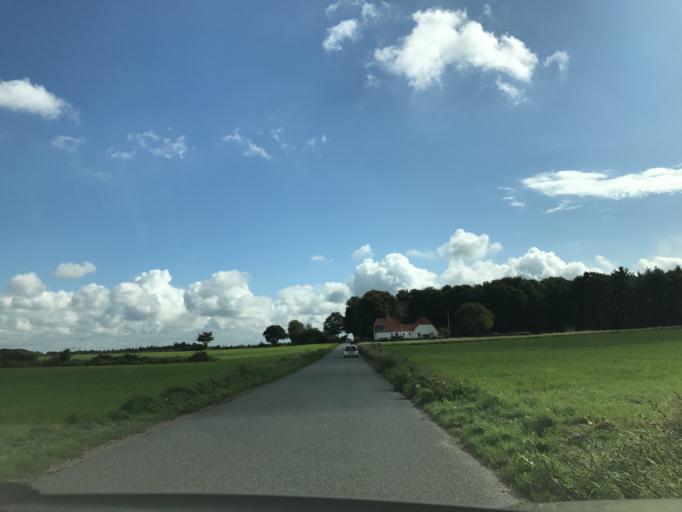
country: DK
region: South Denmark
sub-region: Middelfart Kommune
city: Norre Aby
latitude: 55.4507
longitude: 9.8073
